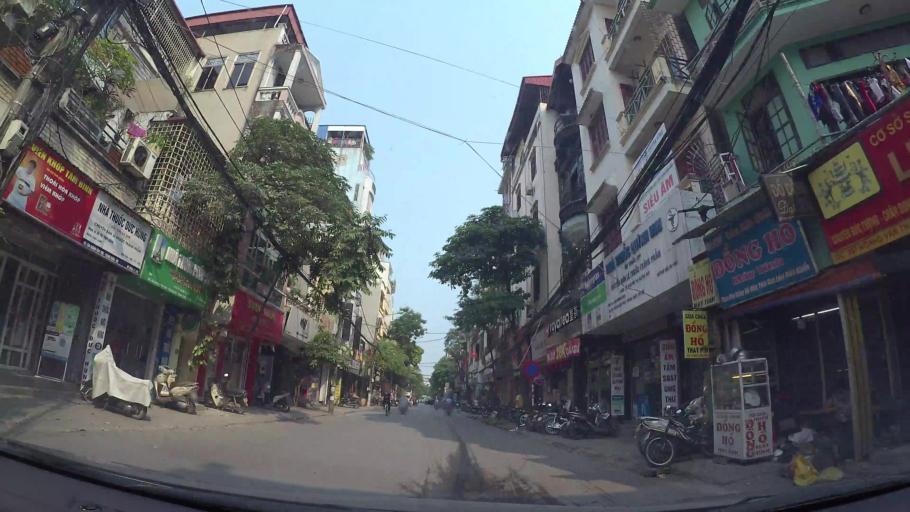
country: VN
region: Ha Noi
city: Thanh Xuan
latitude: 20.9981
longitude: 105.8220
